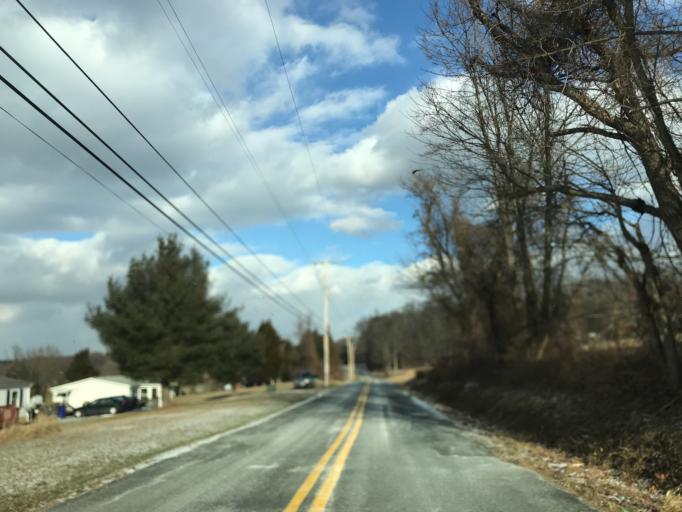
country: US
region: Maryland
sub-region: Harford County
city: Jarrettsville
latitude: 39.6182
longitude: -76.4345
